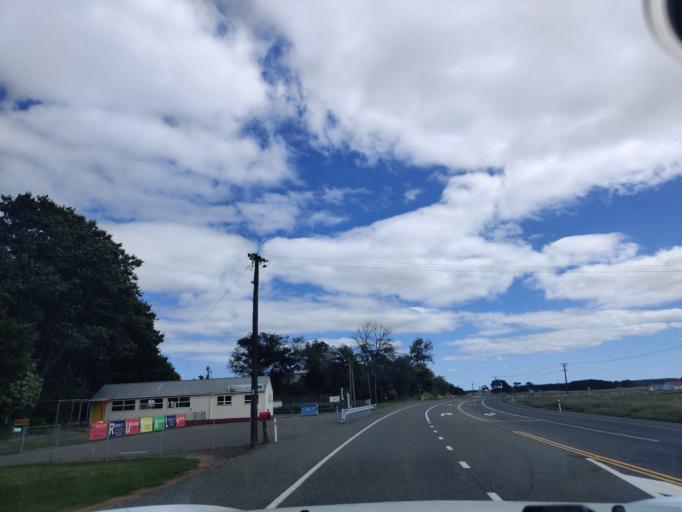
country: NZ
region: Manawatu-Wanganui
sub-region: Horowhenua District
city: Foxton
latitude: -40.4090
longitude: 175.3783
